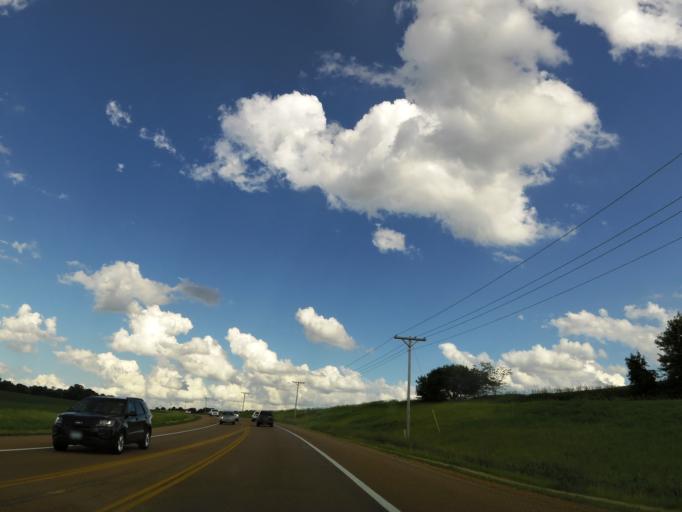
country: US
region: Minnesota
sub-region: Carver County
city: Waconia
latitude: 44.8298
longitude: -93.7585
